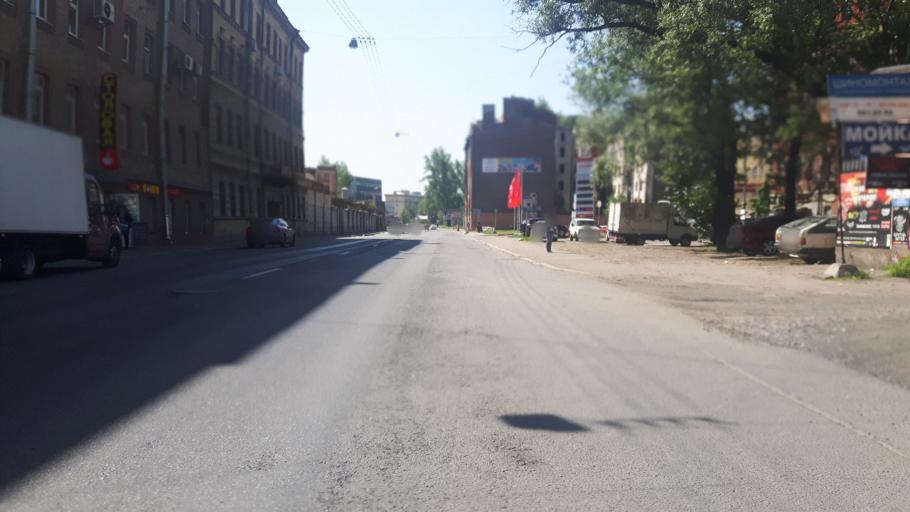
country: RU
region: St.-Petersburg
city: Admiralteisky
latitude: 59.9048
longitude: 30.2883
